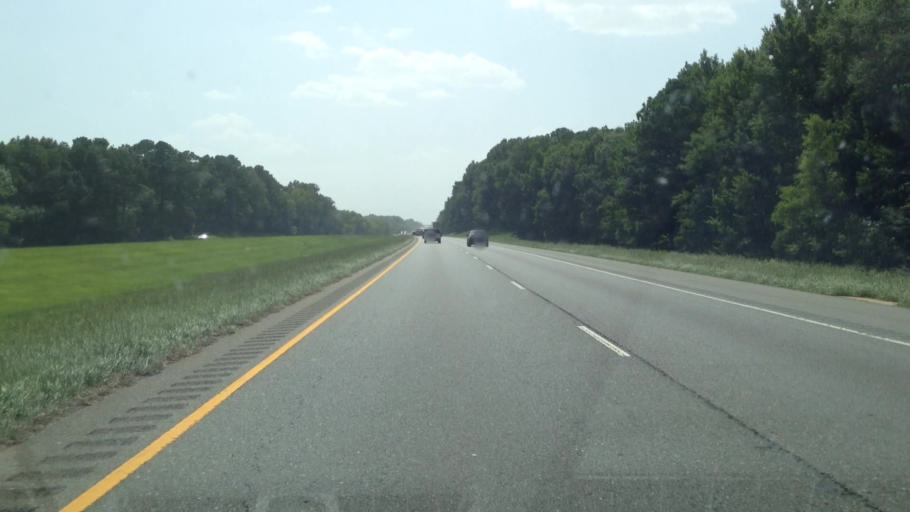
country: US
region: Louisiana
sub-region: Bossier Parish
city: Eastwood
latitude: 32.5423
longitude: -93.5678
